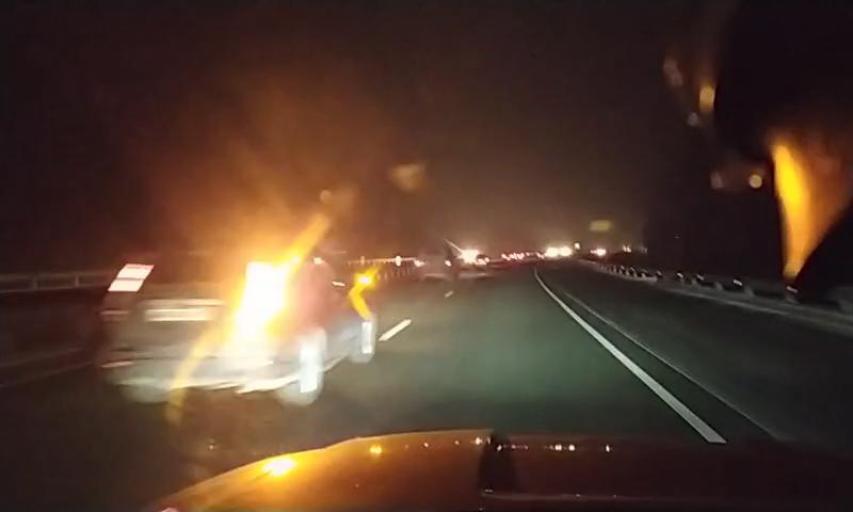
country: RU
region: Leningrad
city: Luppolovo
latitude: 60.1943
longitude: 30.3556
